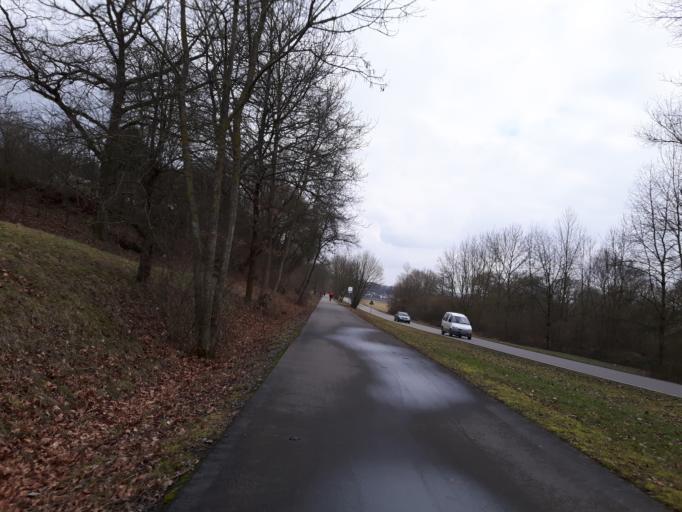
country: DE
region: Baden-Wuerttemberg
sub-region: Regierungsbezirk Stuttgart
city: Neuenstadt am Kocher
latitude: 49.2446
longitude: 9.3826
